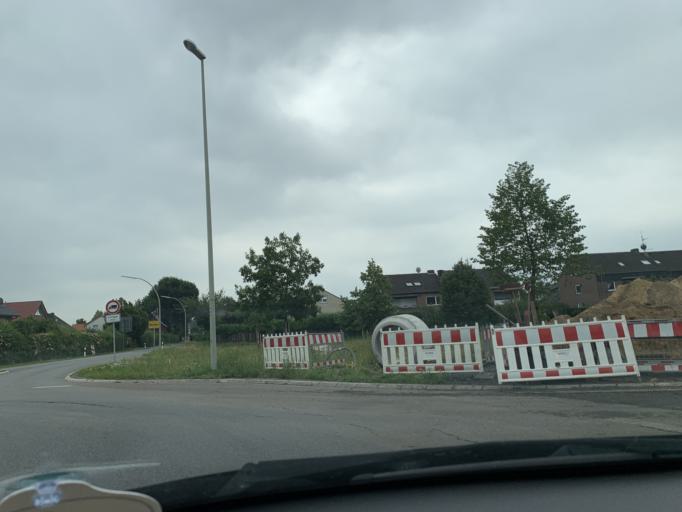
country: DE
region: North Rhine-Westphalia
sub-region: Regierungsbezirk Munster
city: Warendorf
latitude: 51.9632
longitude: 7.9800
